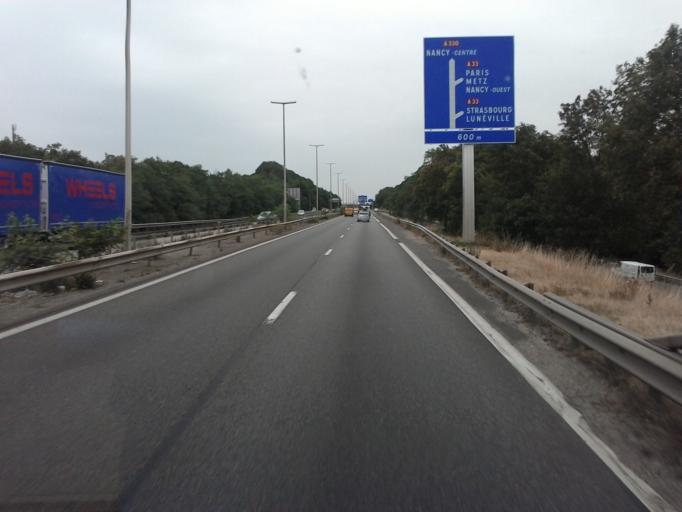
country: FR
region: Lorraine
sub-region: Departement de Meurthe-et-Moselle
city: Ludres
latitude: 48.6175
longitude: 6.1801
